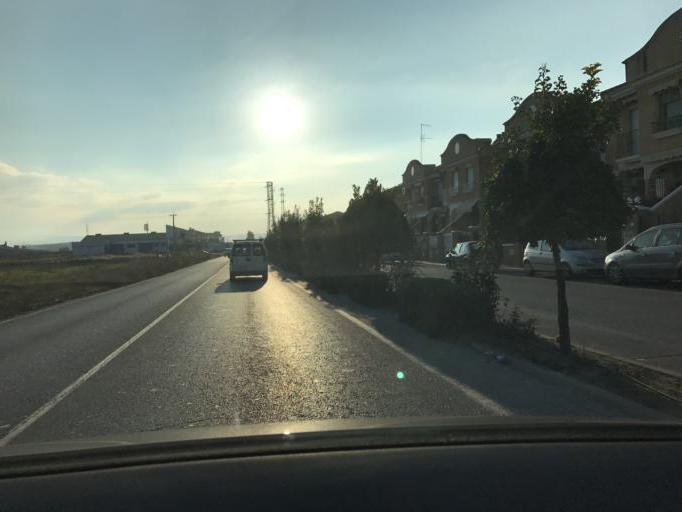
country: ES
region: Andalusia
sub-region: Provincia de Granada
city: Atarfe
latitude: 37.2183
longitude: -3.6865
